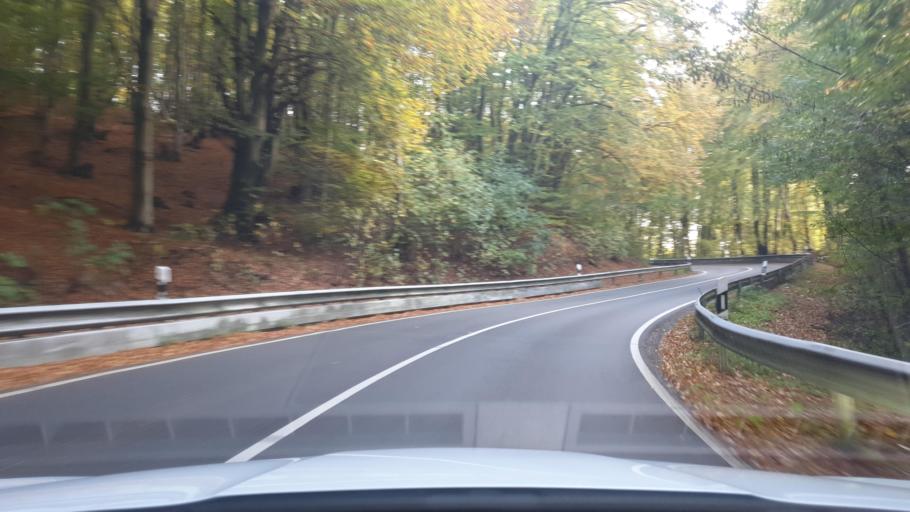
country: DE
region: North Rhine-Westphalia
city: Bad Oeynhausen
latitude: 52.2596
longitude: 8.7977
